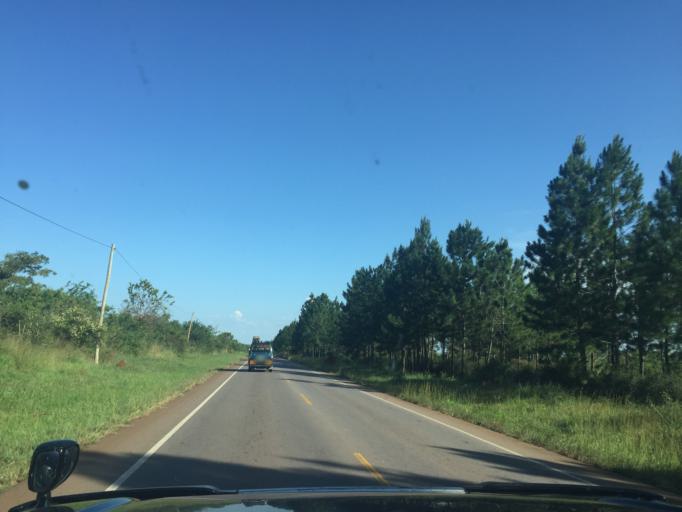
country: UG
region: Central Region
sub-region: Nakasongola District
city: Nakasongola
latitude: 1.3838
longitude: 32.3341
